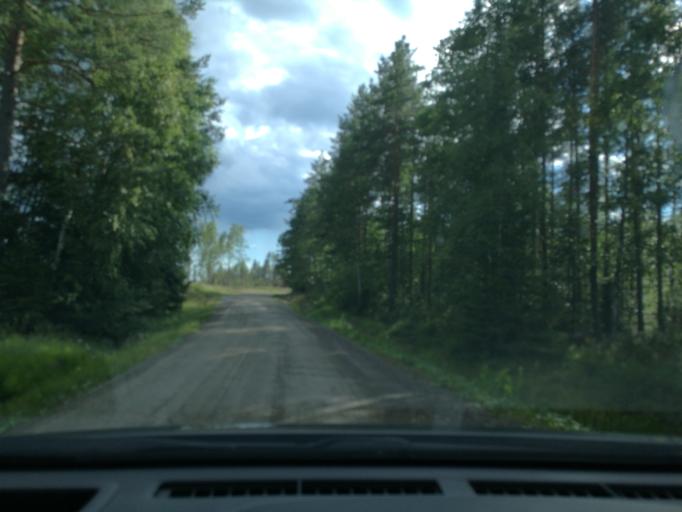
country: SE
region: Vaestmanland
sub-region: Surahammars Kommun
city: Ramnas
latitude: 59.8140
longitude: 16.2398
